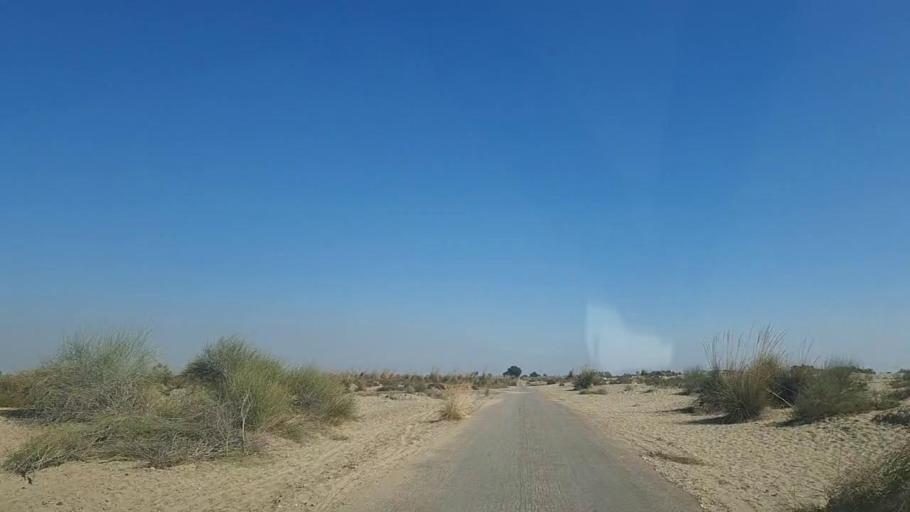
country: PK
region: Sindh
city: Khadro
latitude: 26.2093
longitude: 68.8513
